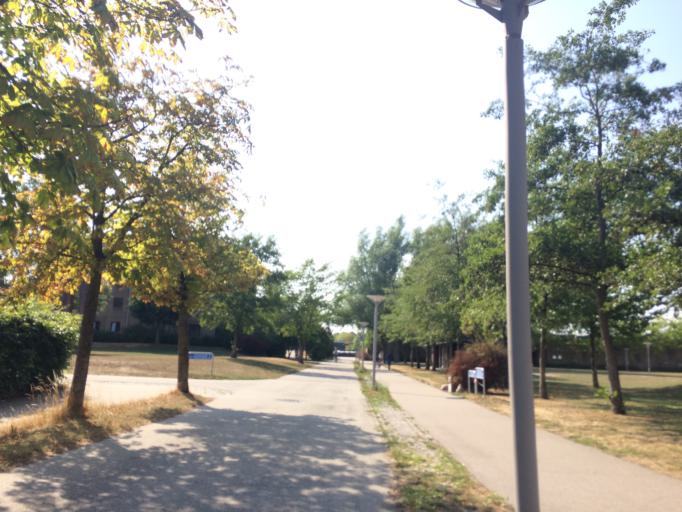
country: DK
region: Capital Region
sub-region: Hvidovre Kommune
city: Hvidovre
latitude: 55.6258
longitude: 12.4527
